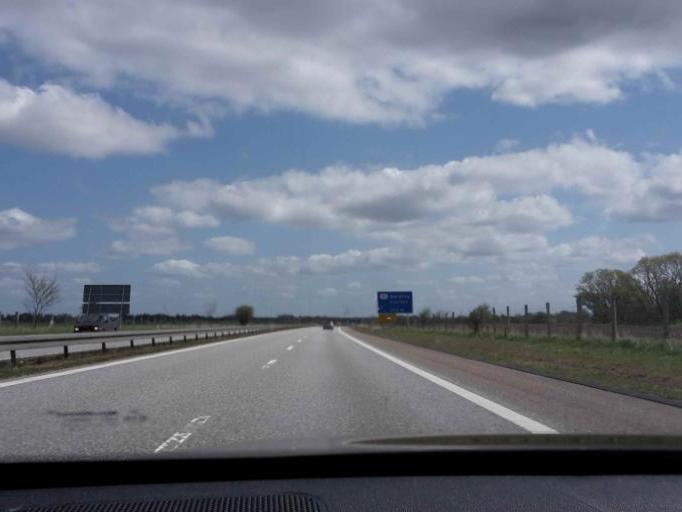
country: DK
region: South Denmark
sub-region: Esbjerg Kommune
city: Bramming
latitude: 55.5139
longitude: 8.7930
